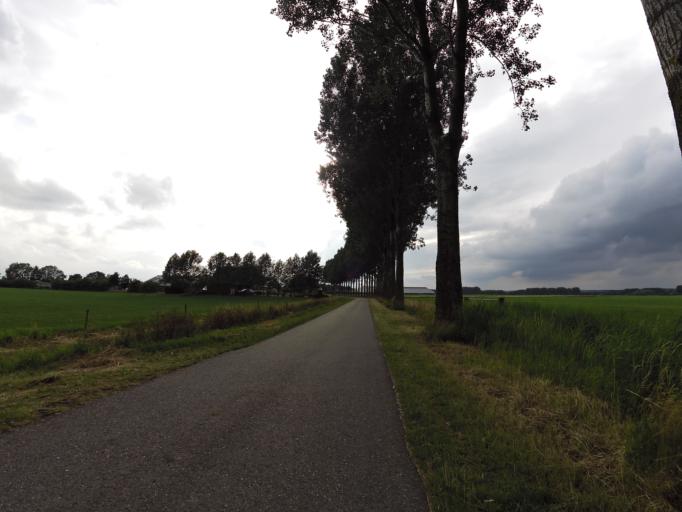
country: NL
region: Gelderland
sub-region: Gemeente Rheden
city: De Steeg
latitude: 51.9815
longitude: 6.0905
